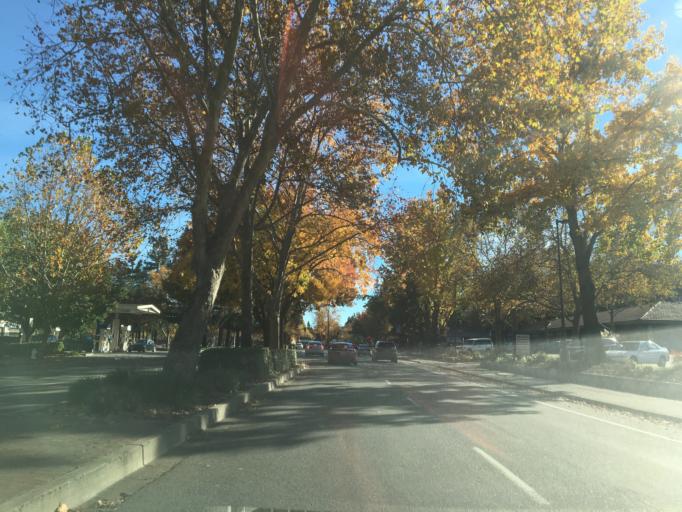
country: US
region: California
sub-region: Contra Costa County
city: Danville
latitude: 37.8149
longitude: -121.9963
